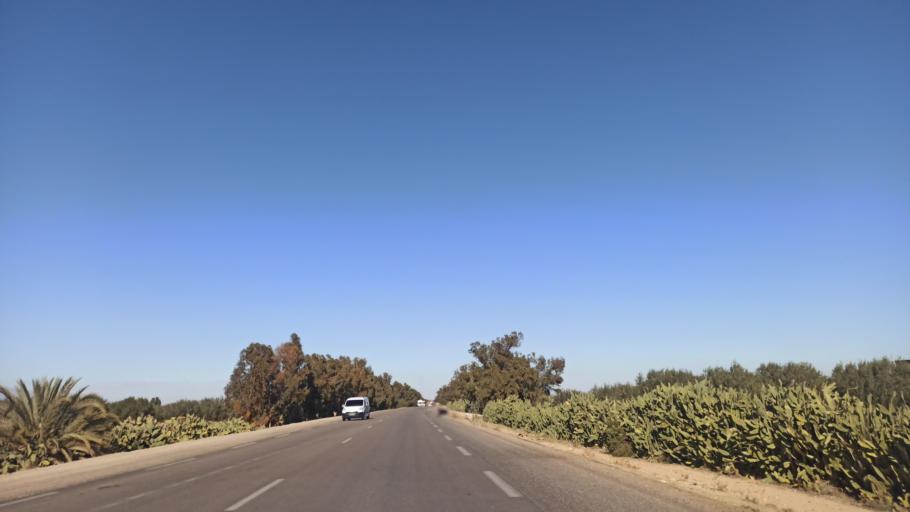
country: TN
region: Sidi Bu Zayd
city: Jilma
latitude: 35.1532
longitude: 9.3648
